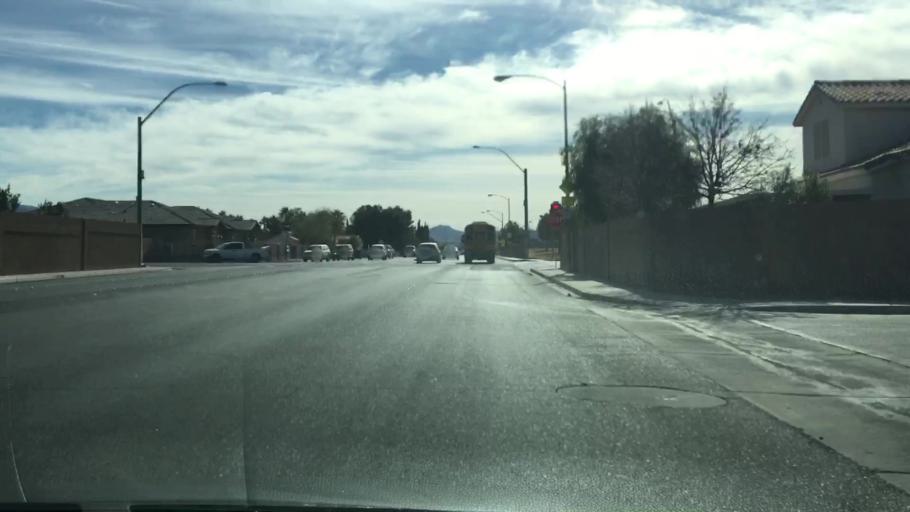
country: US
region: Nevada
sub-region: Clark County
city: Whitney
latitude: 36.0357
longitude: -115.1274
